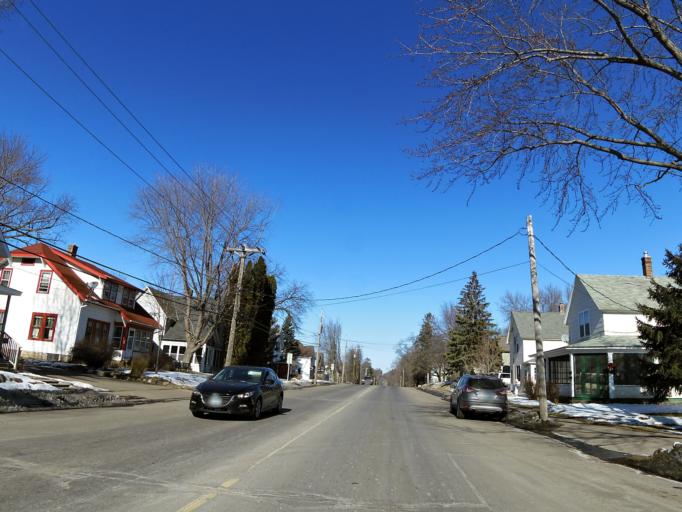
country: US
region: Minnesota
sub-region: Washington County
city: Stillwater
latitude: 45.0551
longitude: -92.8204
